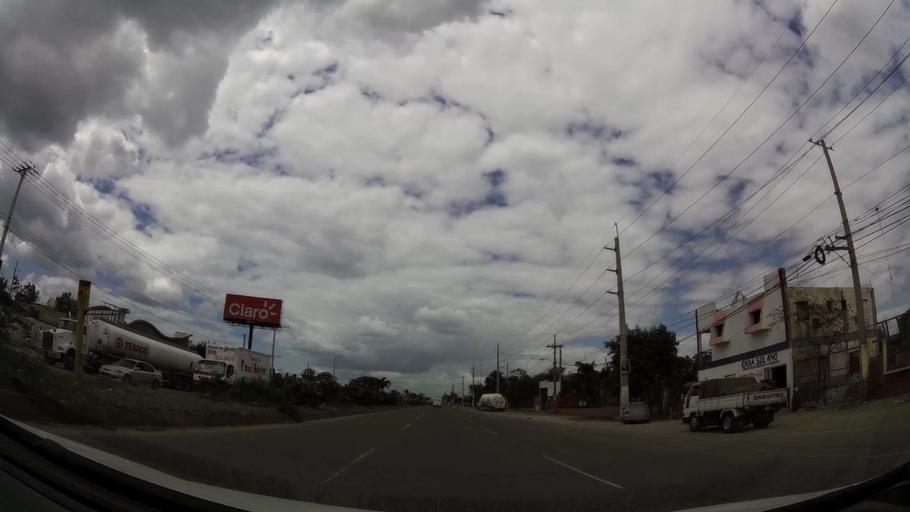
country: DO
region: Santo Domingo
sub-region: Santo Domingo
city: Boca Chica
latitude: 18.4495
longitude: -69.6607
